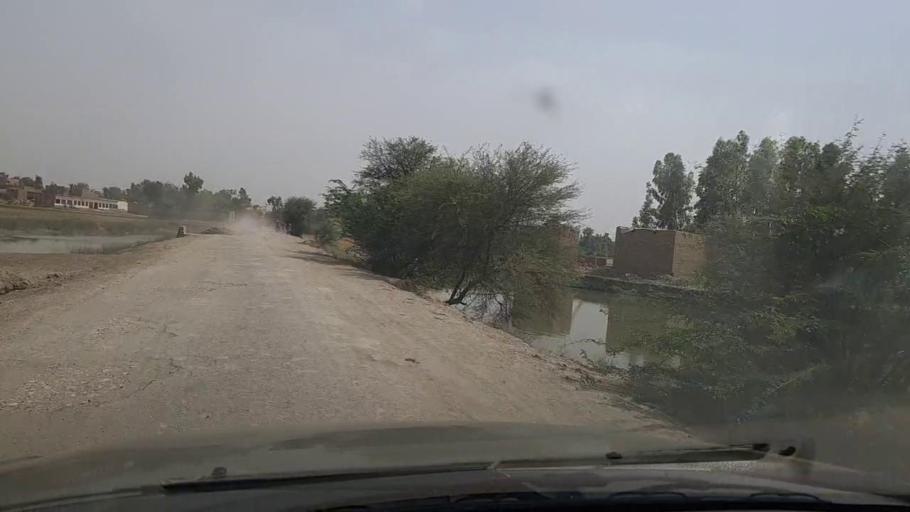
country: PK
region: Sindh
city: Shikarpur
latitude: 27.9143
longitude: 68.6864
